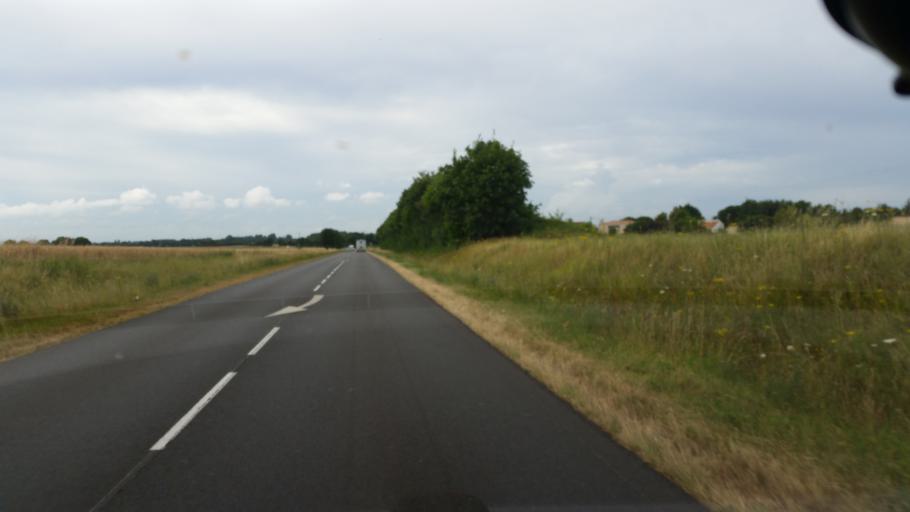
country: FR
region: Poitou-Charentes
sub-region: Departement de la Charente-Maritime
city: Surgeres
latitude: 46.1469
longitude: -0.8068
